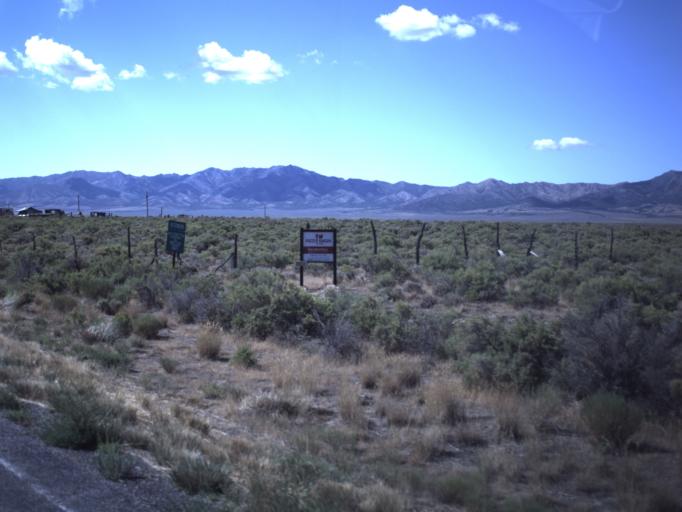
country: US
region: Utah
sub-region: Tooele County
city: Tooele
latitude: 40.1219
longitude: -112.4308
